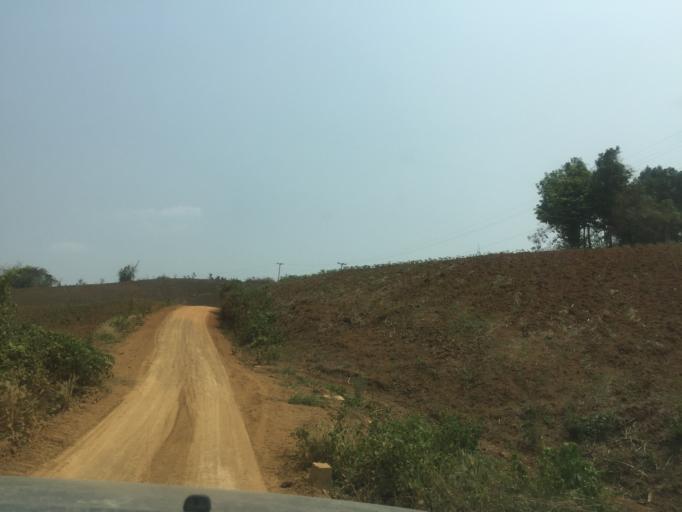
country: LA
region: Xiagnabouli
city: Muang Kenthao
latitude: 17.8017
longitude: 101.2683
